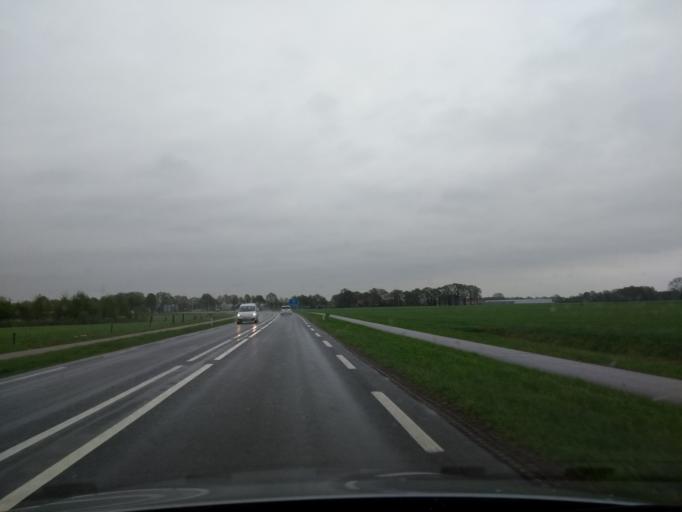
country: NL
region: Overijssel
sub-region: Gemeente Tubbergen
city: Tubbergen
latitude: 52.3783
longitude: 6.7978
